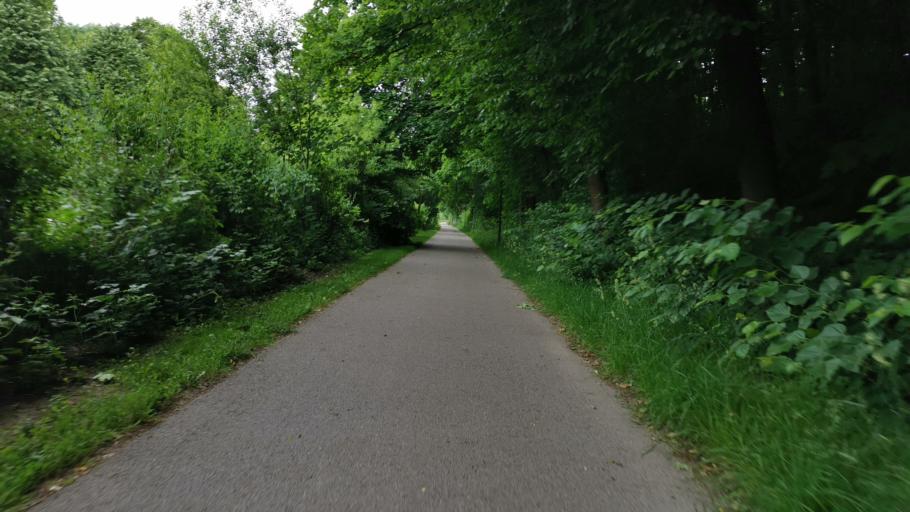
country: DE
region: Bavaria
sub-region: Upper Bavaria
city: Neuried
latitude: 48.0948
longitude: 11.4619
